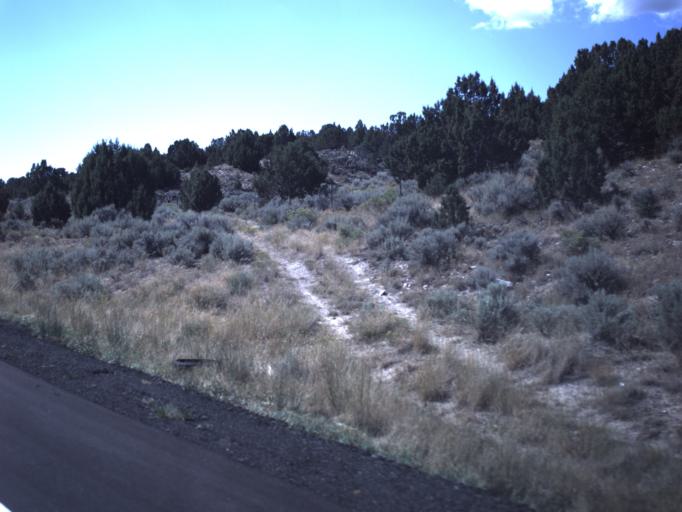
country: US
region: Utah
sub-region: Utah County
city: Eagle Mountain
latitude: 40.0157
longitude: -112.2783
